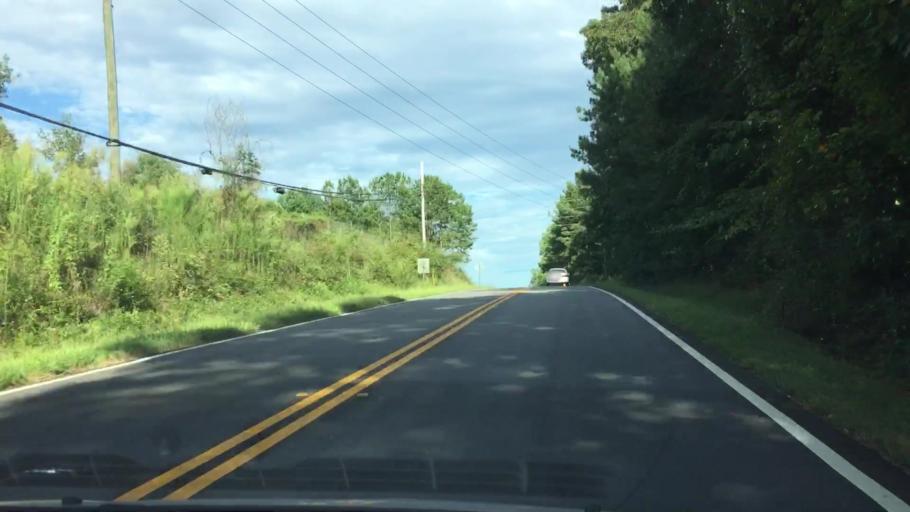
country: US
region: Georgia
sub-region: Henry County
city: Stockbridge
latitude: 33.5813
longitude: -84.1805
